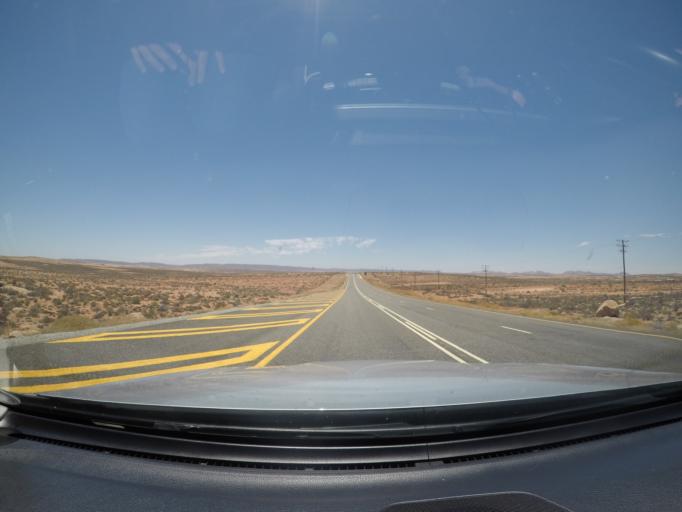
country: ZA
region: Northern Cape
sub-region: Namakwa District Municipality
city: Springbok
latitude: -29.3815
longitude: 17.7990
